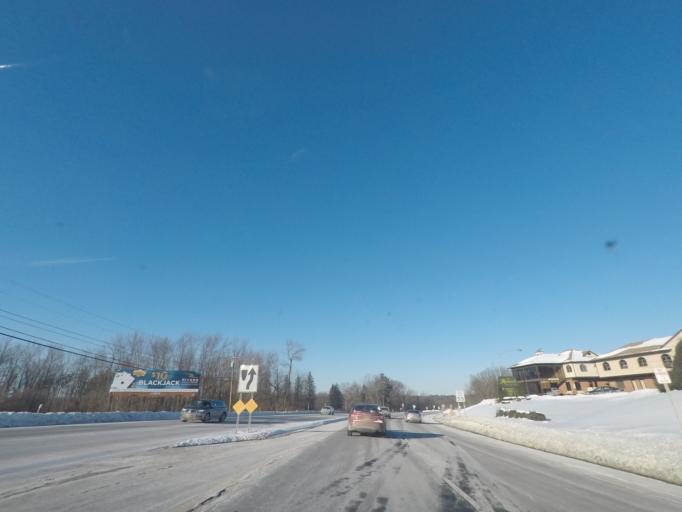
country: US
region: New York
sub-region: Saratoga County
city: Saratoga Springs
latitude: 43.0272
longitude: -73.7924
